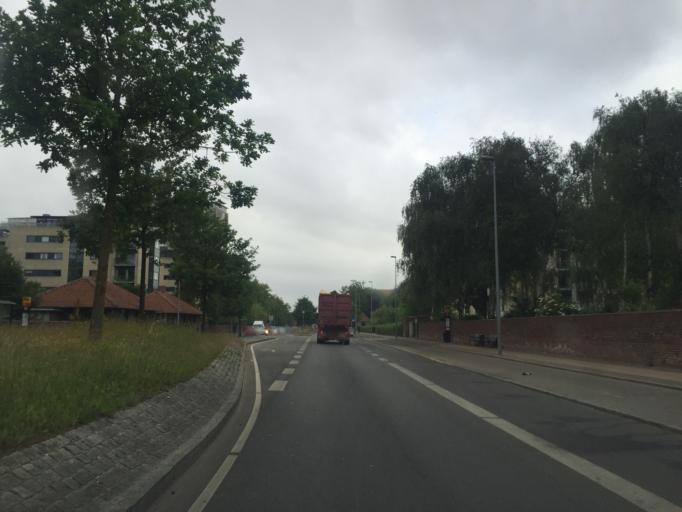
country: DK
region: Capital Region
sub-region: Frederiksberg Kommune
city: Frederiksberg
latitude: 55.6722
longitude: 12.5107
